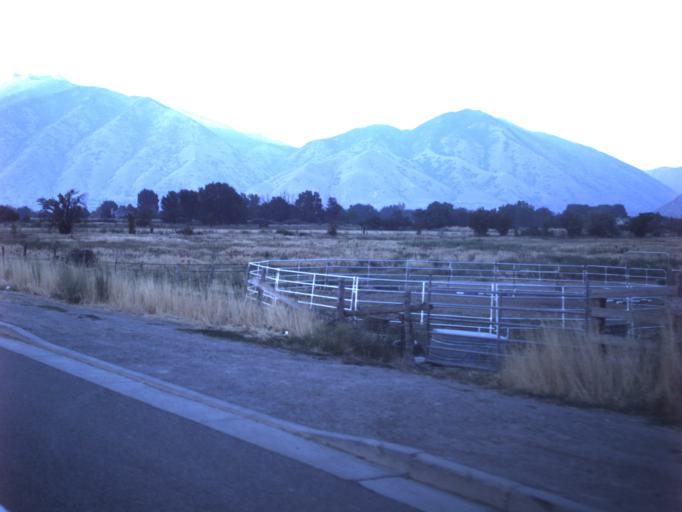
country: US
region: Utah
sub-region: Utah County
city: Mapleton
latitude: 40.1245
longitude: -111.5977
